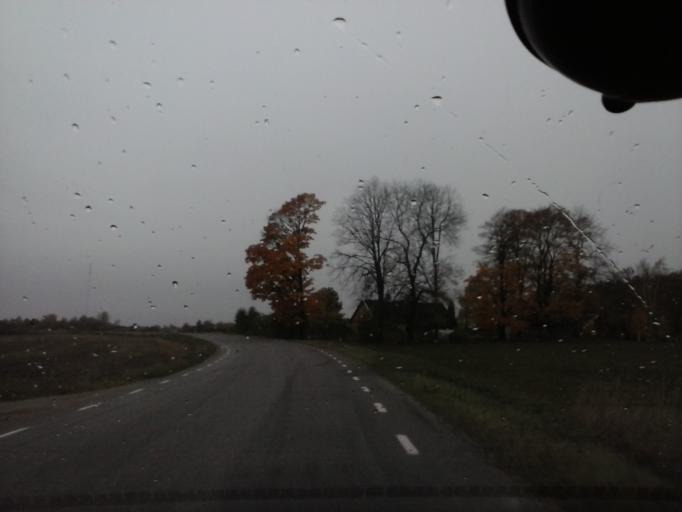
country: EE
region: Viljandimaa
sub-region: Vohma linn
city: Vohma
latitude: 58.6878
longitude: 25.6609
